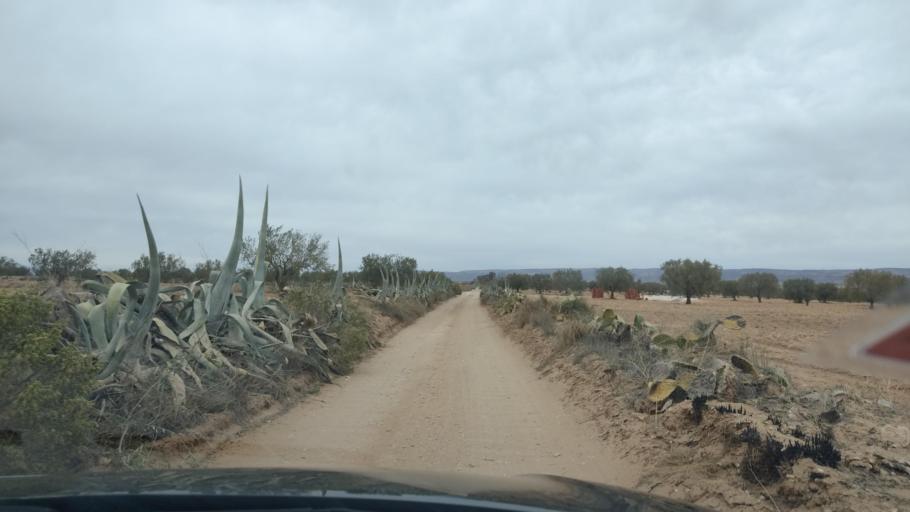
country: TN
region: Al Qasrayn
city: Kasserine
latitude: 35.2246
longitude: 8.9366
